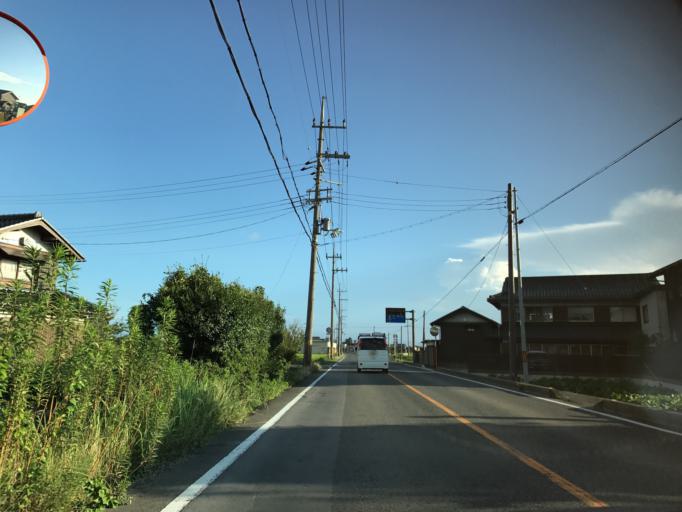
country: JP
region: Shiga Prefecture
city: Youkaichi
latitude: 35.1347
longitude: 136.2620
